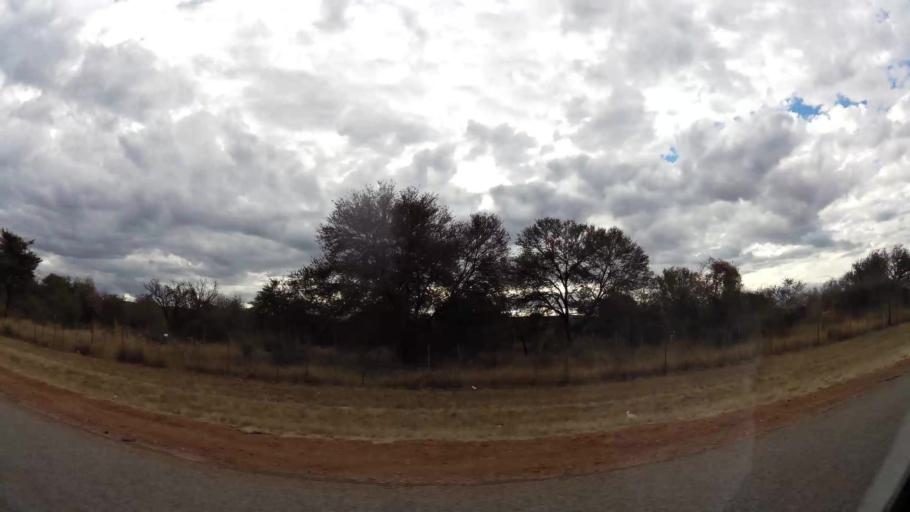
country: ZA
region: Limpopo
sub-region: Waterberg District Municipality
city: Modimolle
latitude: -24.5305
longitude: 28.7036
